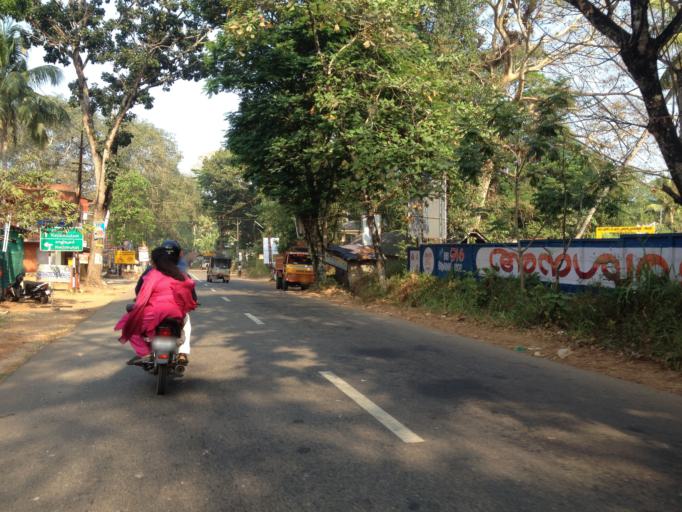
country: IN
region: Kerala
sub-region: Pattanamtitta
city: Adur
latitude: 9.1603
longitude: 76.7158
